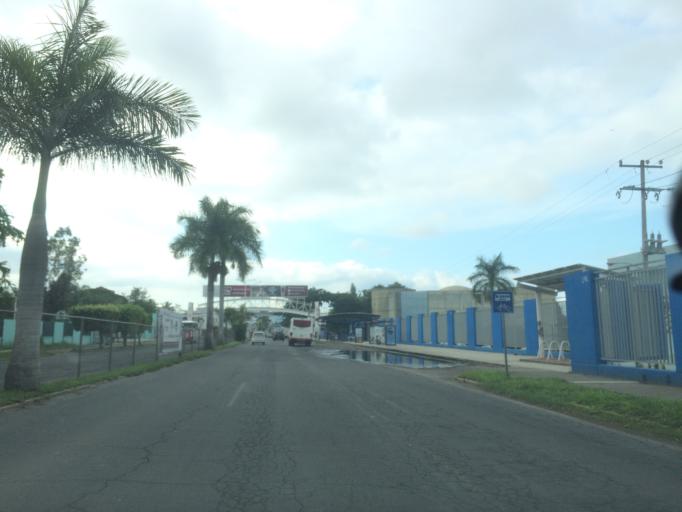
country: MX
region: Nayarit
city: Tepic
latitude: 21.4898
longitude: -104.8949
